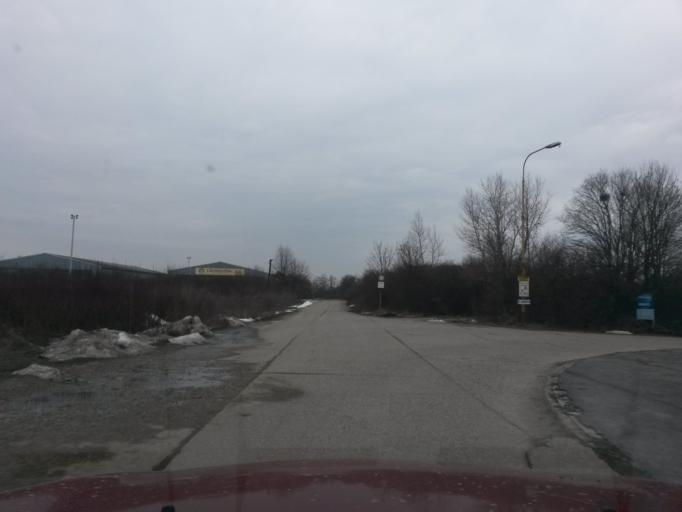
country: SK
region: Kosicky
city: Michalovce
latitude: 48.7523
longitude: 21.8857
